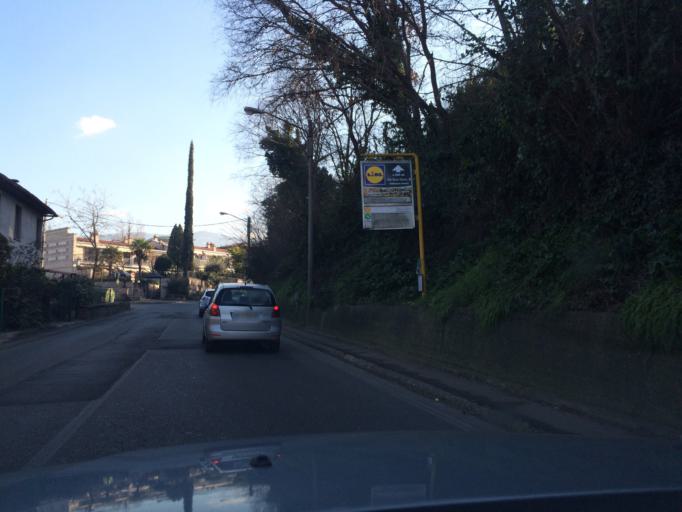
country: IT
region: Umbria
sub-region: Provincia di Terni
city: Terni
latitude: 42.5570
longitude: 12.6578
